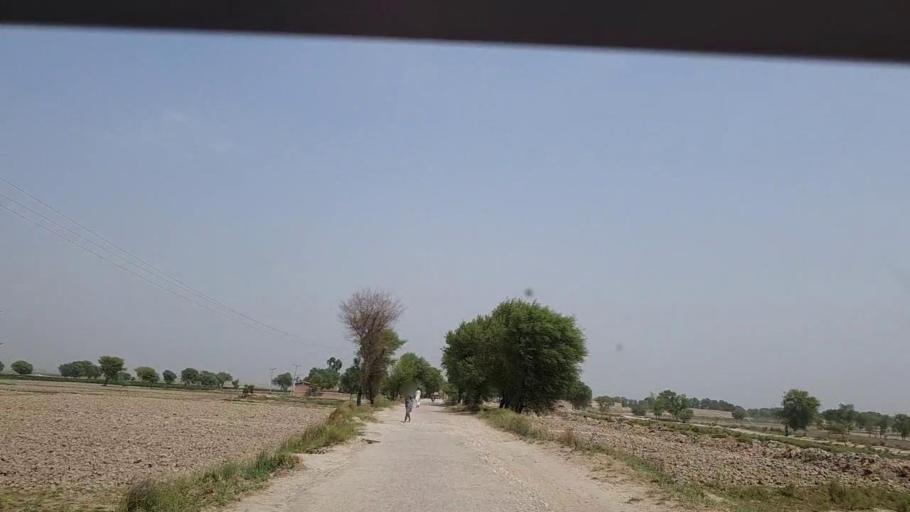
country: PK
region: Sindh
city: Khairpur Nathan Shah
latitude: 27.0786
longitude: 67.6847
